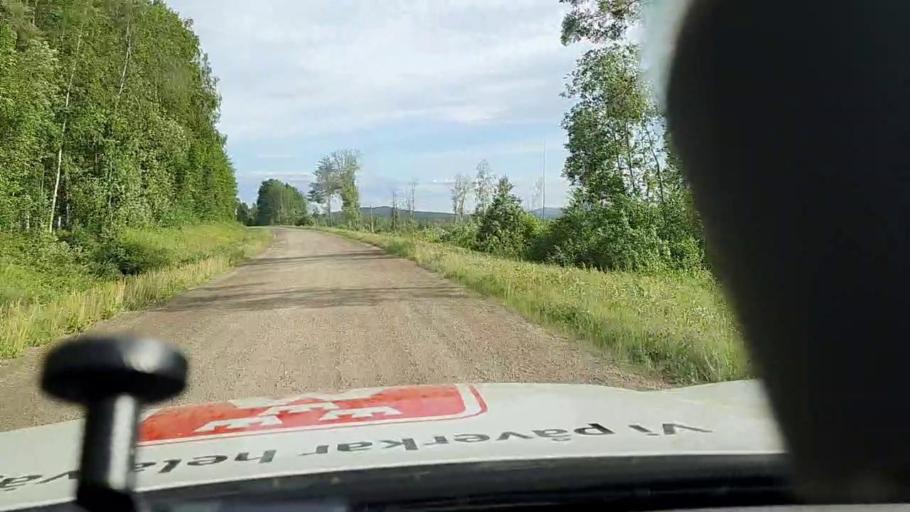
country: SE
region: Norrbotten
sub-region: Alvsbyns Kommun
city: AElvsbyn
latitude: 66.1912
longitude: 21.1957
